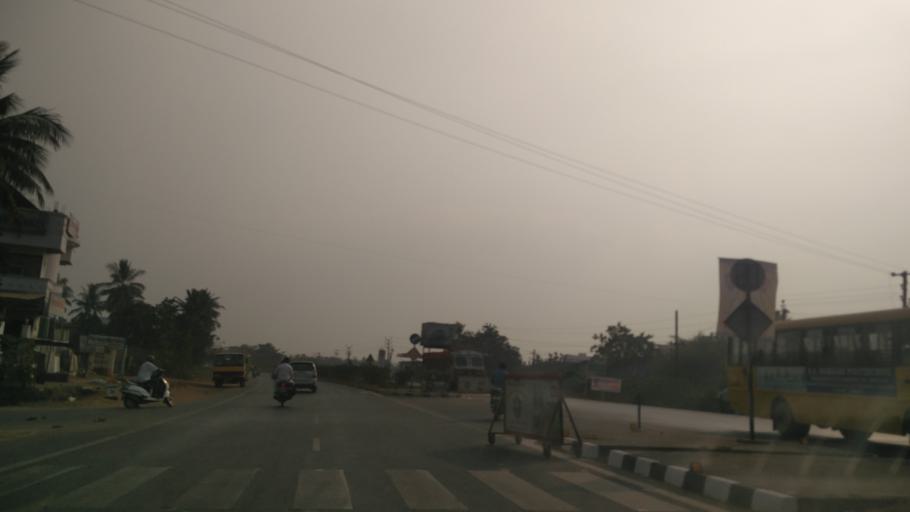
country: IN
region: Andhra Pradesh
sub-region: East Godavari
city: Rajahmundry
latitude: 16.9859
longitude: 81.7987
